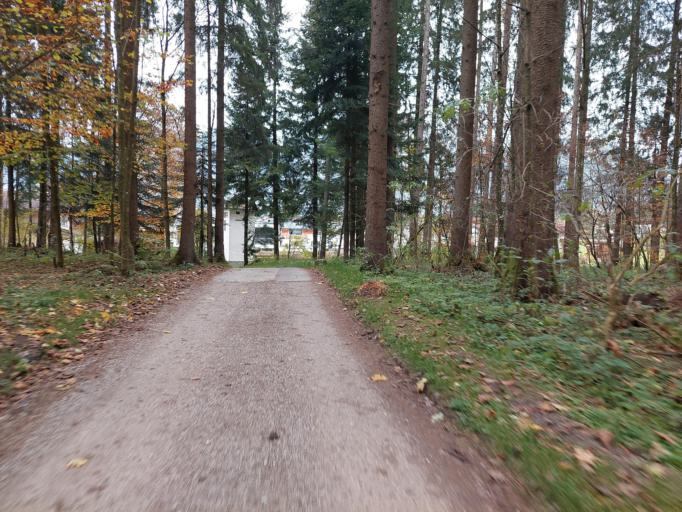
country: AT
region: Tyrol
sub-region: Politischer Bezirk Kufstein
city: Angath
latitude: 47.5049
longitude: 12.0414
